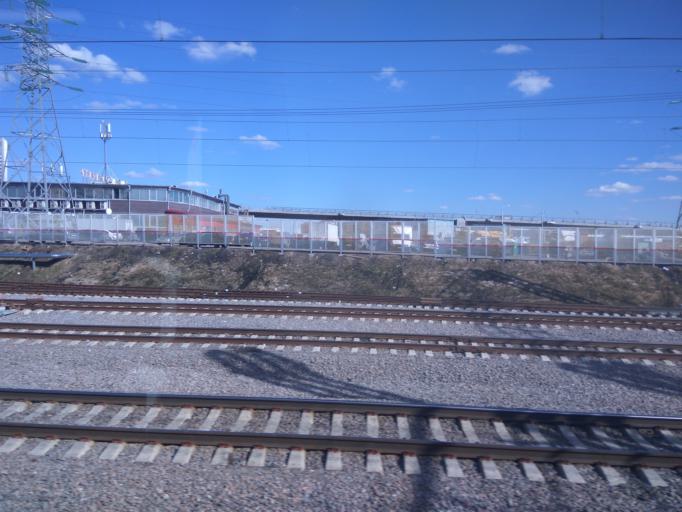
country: RU
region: Moskovskaya
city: Bogorodskoye
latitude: 55.7988
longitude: 37.7463
